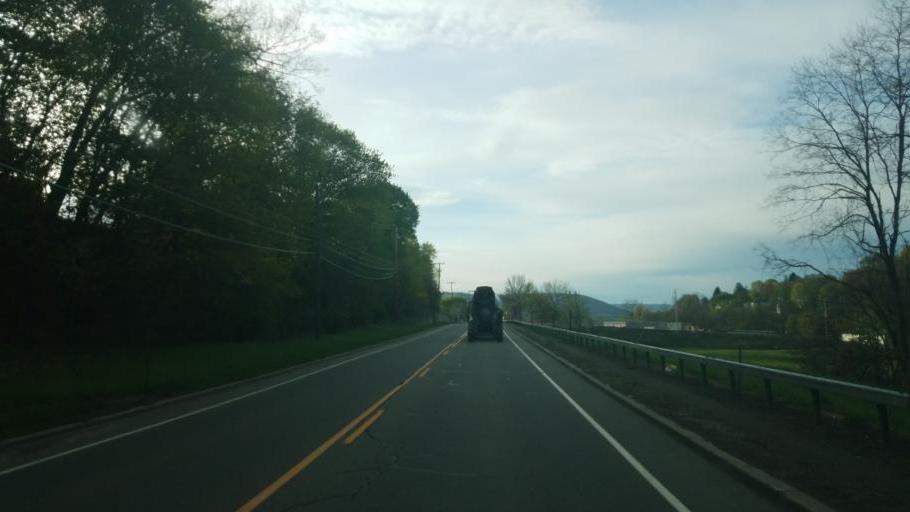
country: US
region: New York
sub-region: Steuben County
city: Hornell
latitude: 42.3325
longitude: -77.6721
